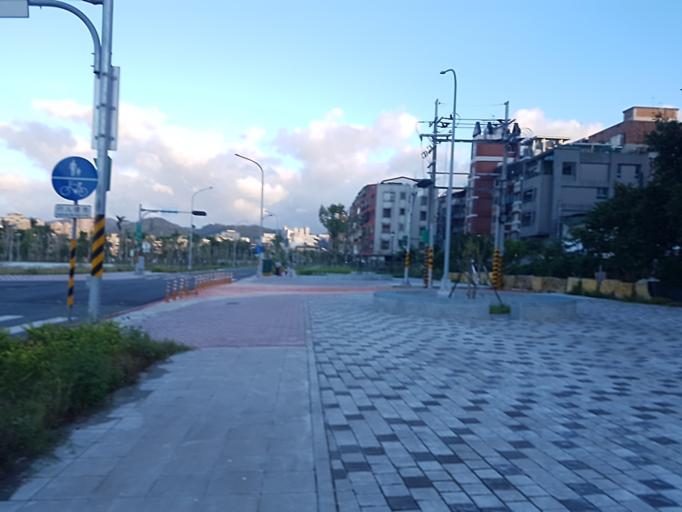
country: TW
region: Taipei
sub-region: Taipei
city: Banqiao
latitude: 24.9776
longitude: 121.5271
